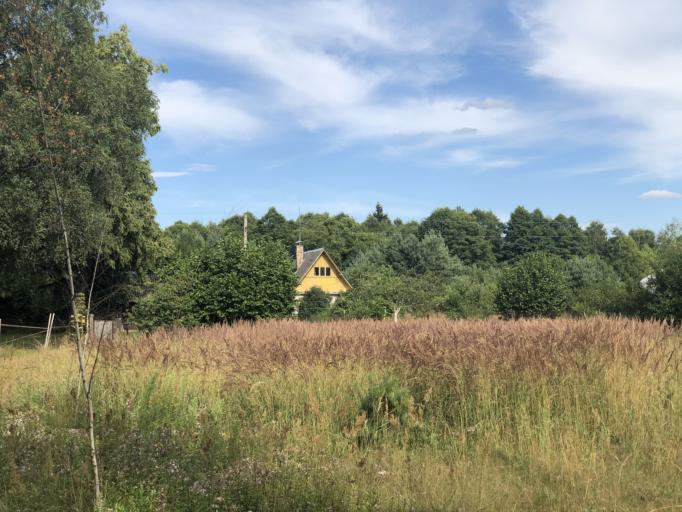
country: BY
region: Grodnenskaya
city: Skidal'
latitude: 53.8239
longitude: 24.1798
